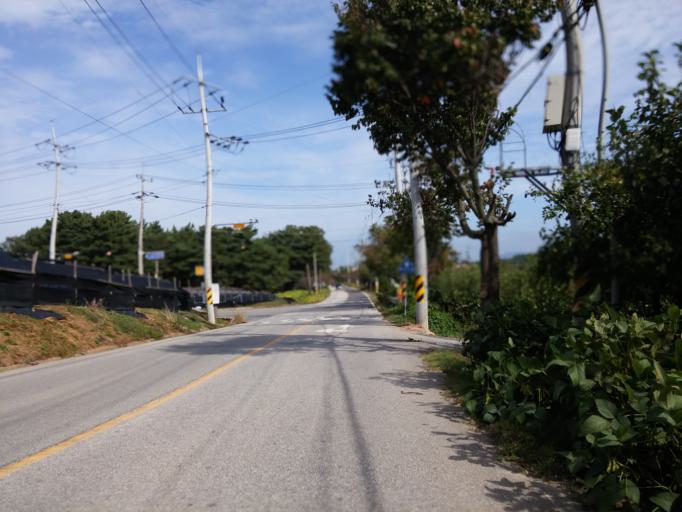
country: KR
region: Chungcheongnam-do
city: Nonsan
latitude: 36.1724
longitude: 127.1175
